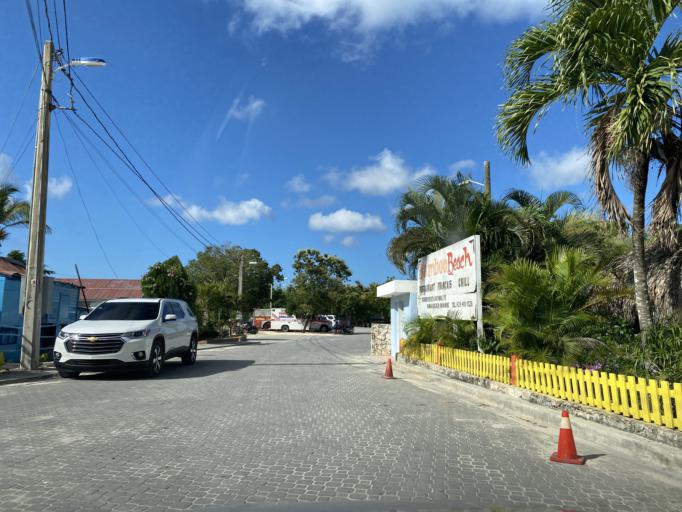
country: DO
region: La Romana
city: La Romana
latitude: 18.3692
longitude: -68.8407
